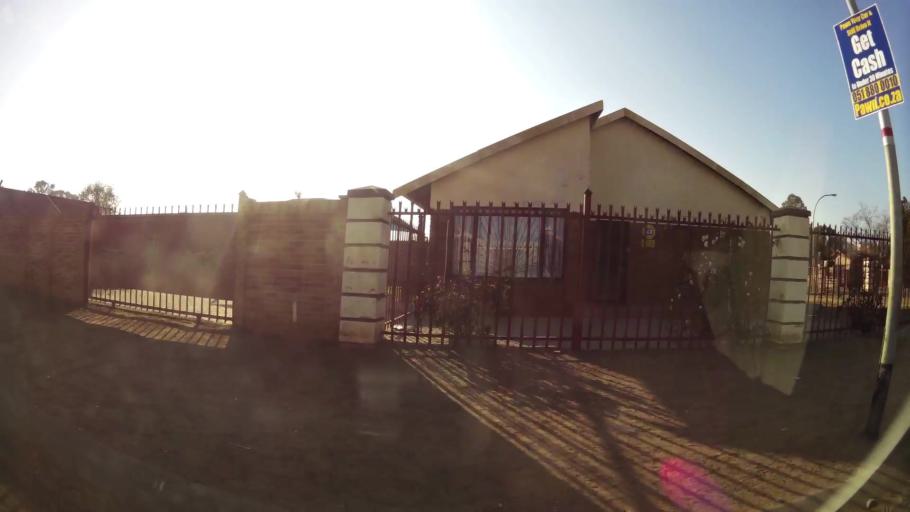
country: ZA
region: Orange Free State
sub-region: Mangaung Metropolitan Municipality
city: Bloemfontein
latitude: -29.1545
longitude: 26.2156
